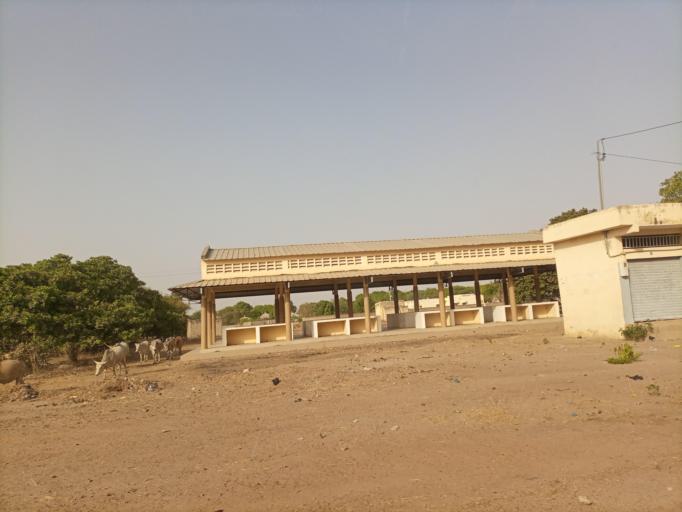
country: SN
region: Fatick
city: Passi
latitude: 14.0197
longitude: -16.2954
